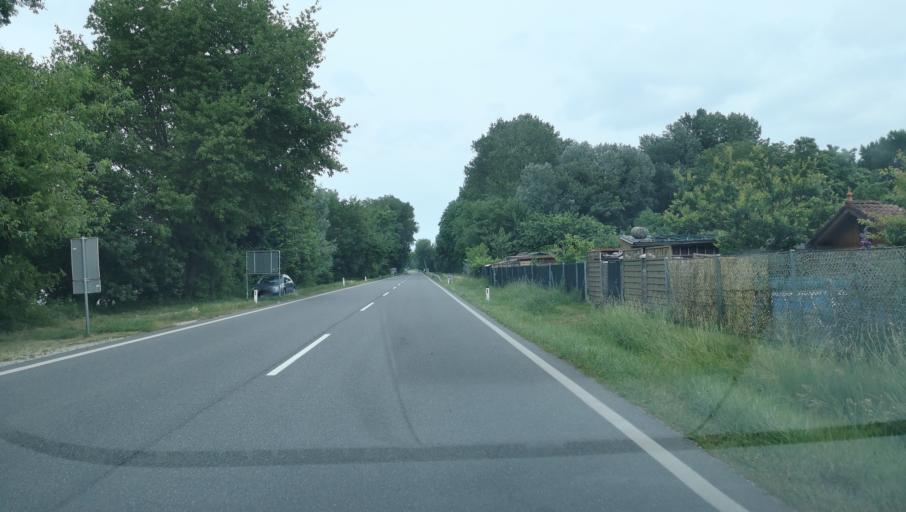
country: AT
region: Lower Austria
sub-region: Politischer Bezirk Krems
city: Weinzierl bei Krems
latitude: 48.3905
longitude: 15.5632
